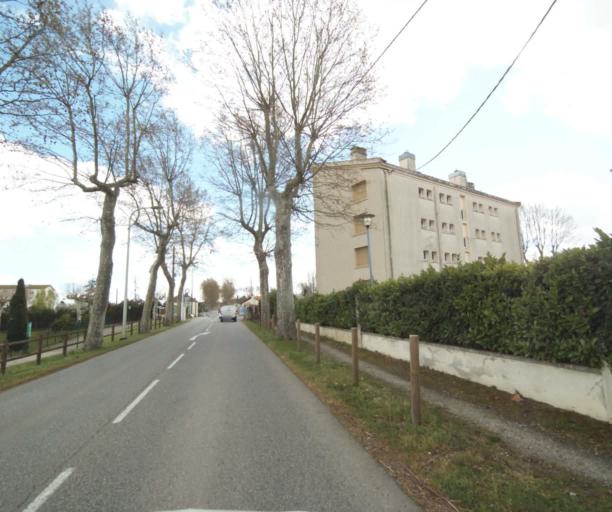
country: FR
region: Midi-Pyrenees
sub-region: Departement de l'Ariege
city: Saverdun
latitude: 43.2399
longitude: 1.5724
